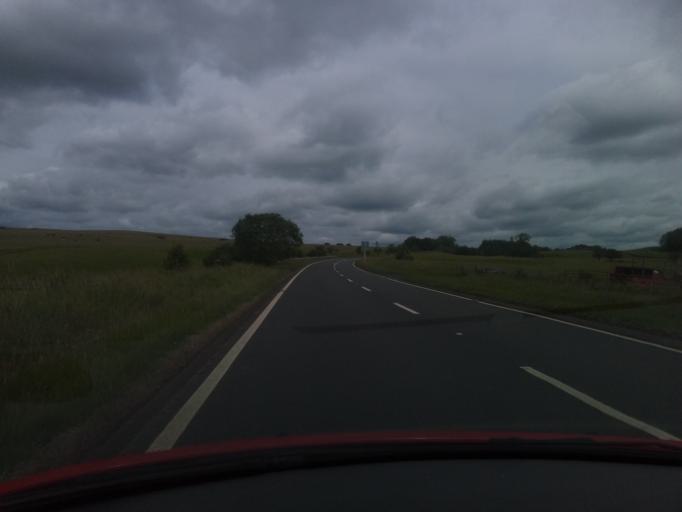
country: GB
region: Scotland
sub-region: The Scottish Borders
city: Hawick
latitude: 55.4525
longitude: -2.7791
